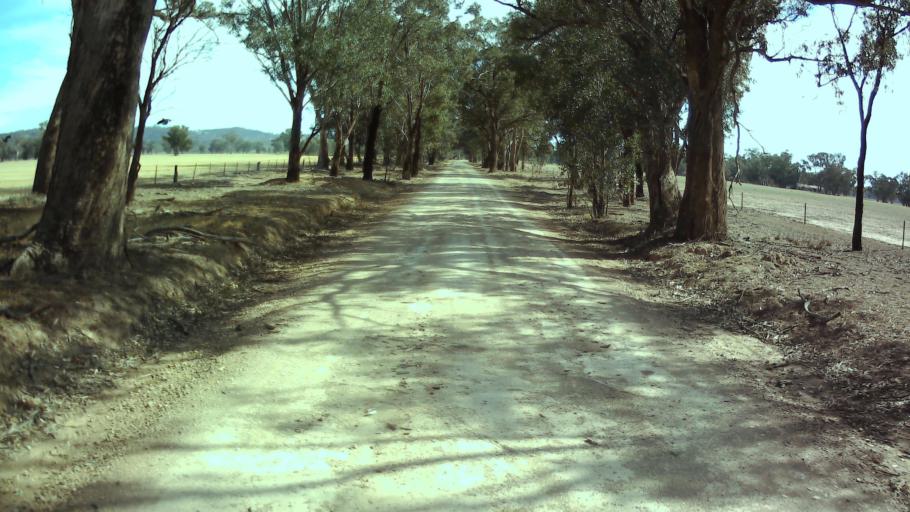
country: AU
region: New South Wales
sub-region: Weddin
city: Grenfell
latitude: -33.6983
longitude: 148.3026
